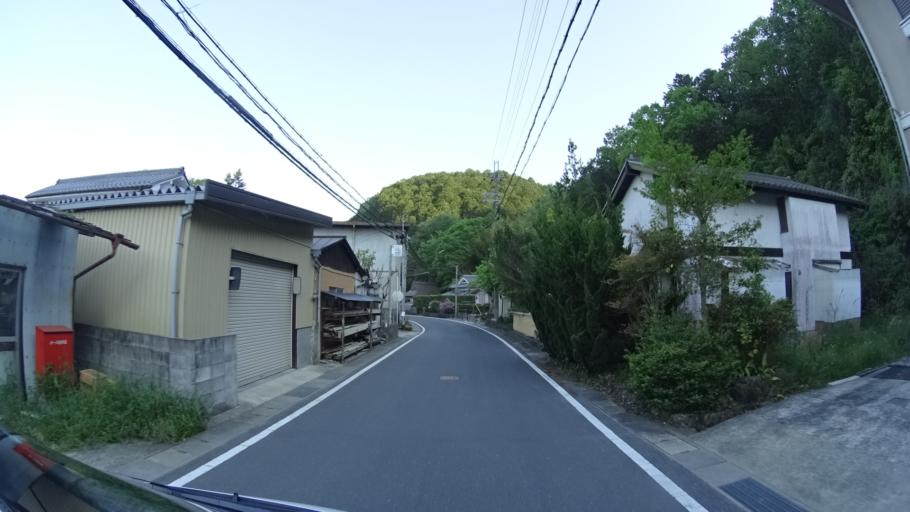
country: JP
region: Kyoto
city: Kameoka
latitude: 35.0864
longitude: 135.5140
